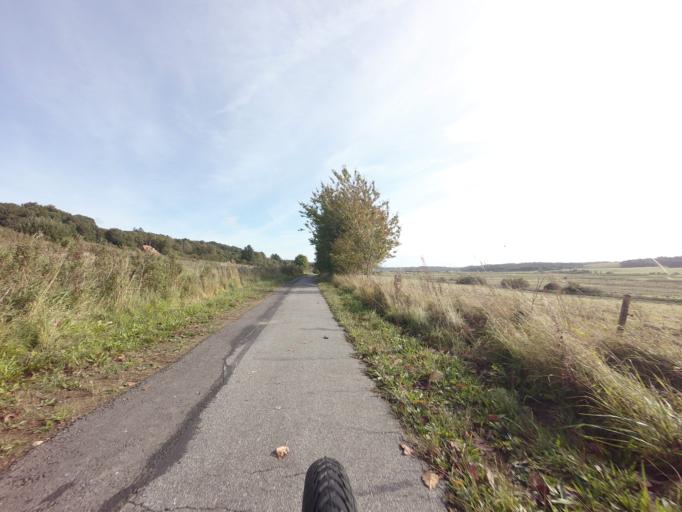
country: DK
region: Central Jutland
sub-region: Viborg Kommune
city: Viborg
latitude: 56.4388
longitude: 9.5094
